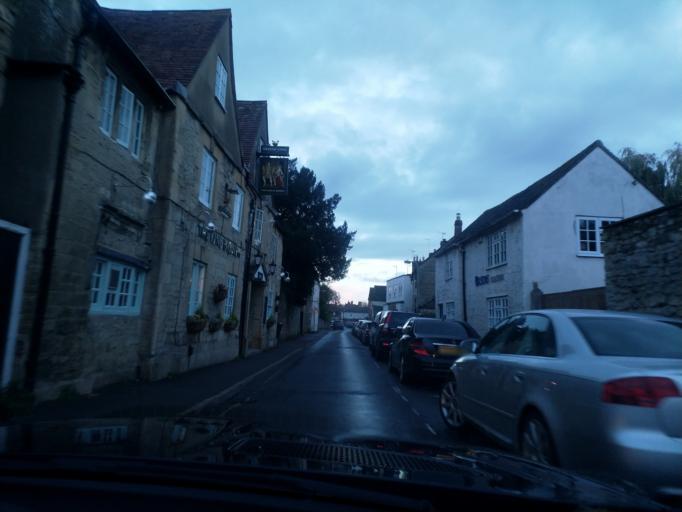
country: GB
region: England
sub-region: Oxfordshire
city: Wheatley
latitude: 51.7473
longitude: -1.1391
